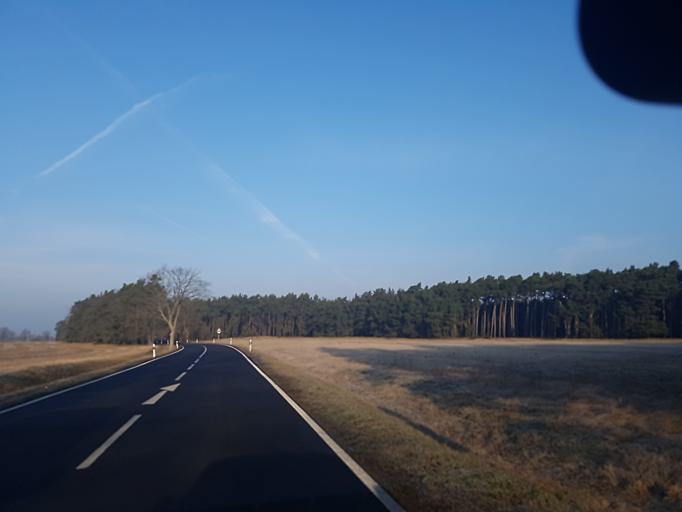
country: DE
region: Brandenburg
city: Golzow
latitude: 52.2695
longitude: 12.6433
